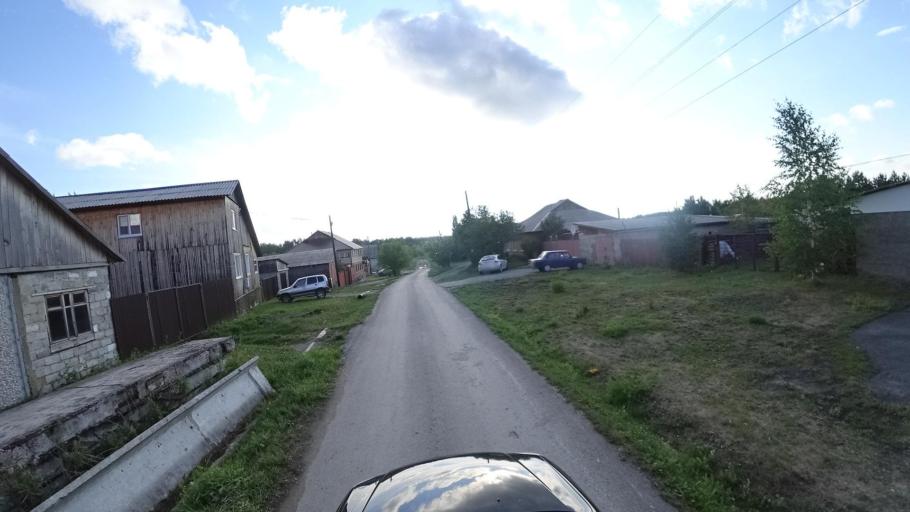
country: RU
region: Sverdlovsk
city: Obukhovskoye
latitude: 56.8510
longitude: 62.6512
